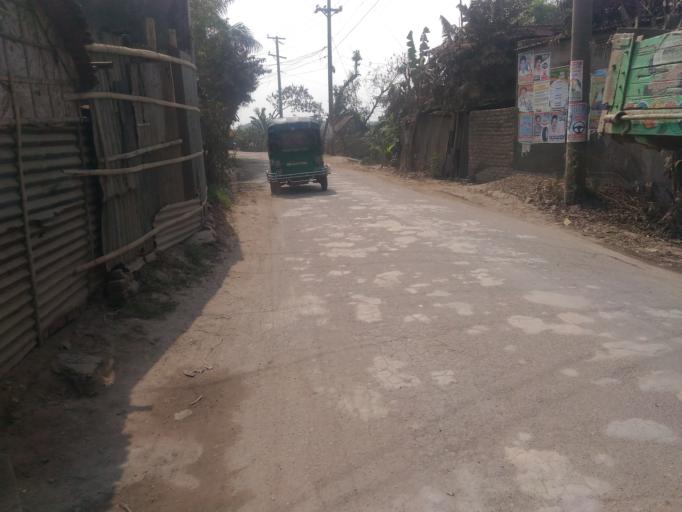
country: BD
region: Dhaka
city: Narayanganj
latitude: 23.6537
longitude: 90.4473
